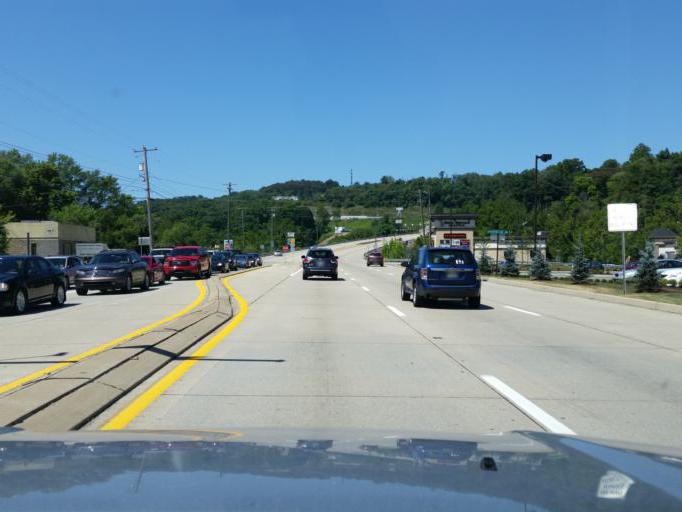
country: US
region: Pennsylvania
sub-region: Westmoreland County
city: Murrysville
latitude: 40.4271
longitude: -79.6996
